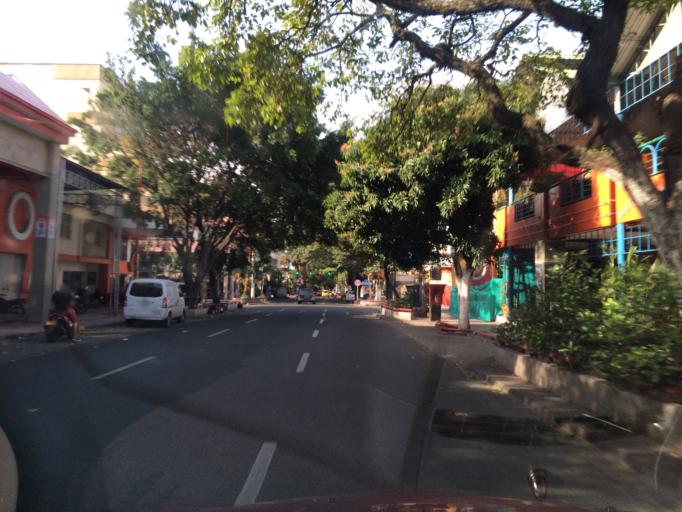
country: CO
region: Valle del Cauca
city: Cali
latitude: 3.4588
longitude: -76.5325
